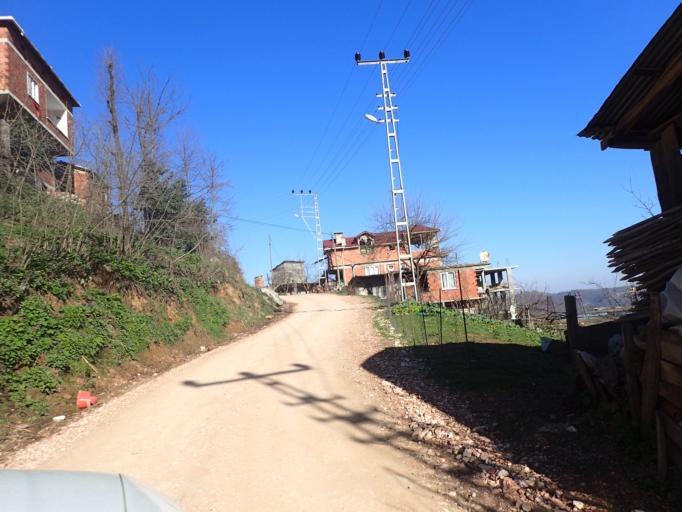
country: TR
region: Ordu
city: Camas
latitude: 40.8715
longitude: 37.5003
